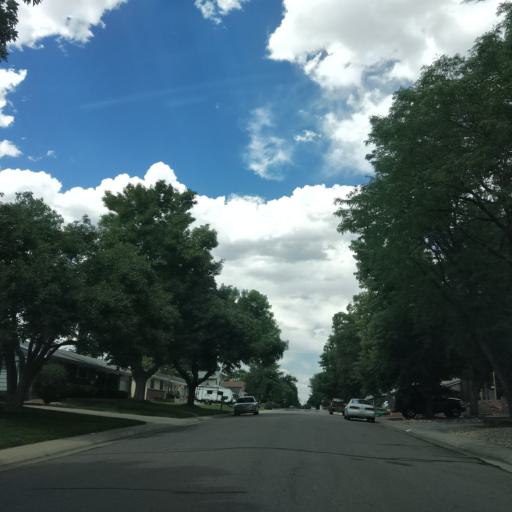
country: US
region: Colorado
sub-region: Jefferson County
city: Lakewood
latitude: 39.6840
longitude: -105.0993
